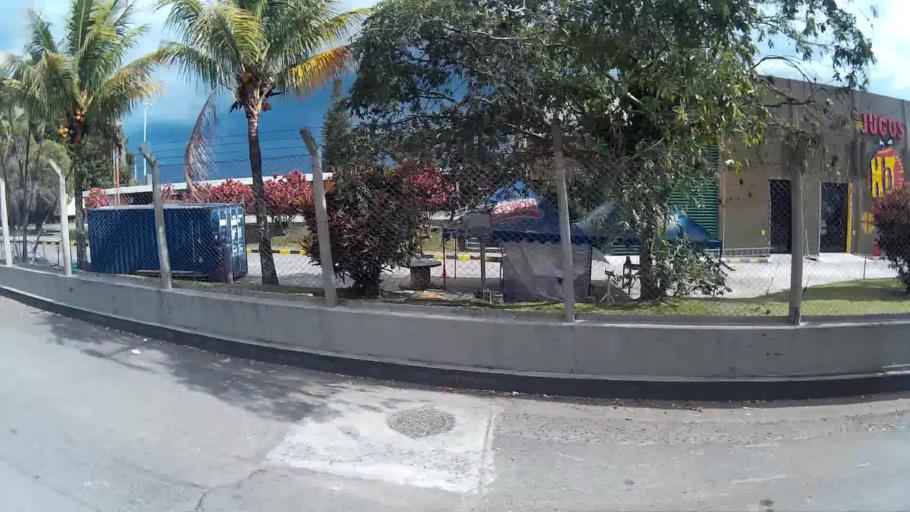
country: CO
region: Risaralda
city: Pereira
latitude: 4.8130
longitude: -75.7605
